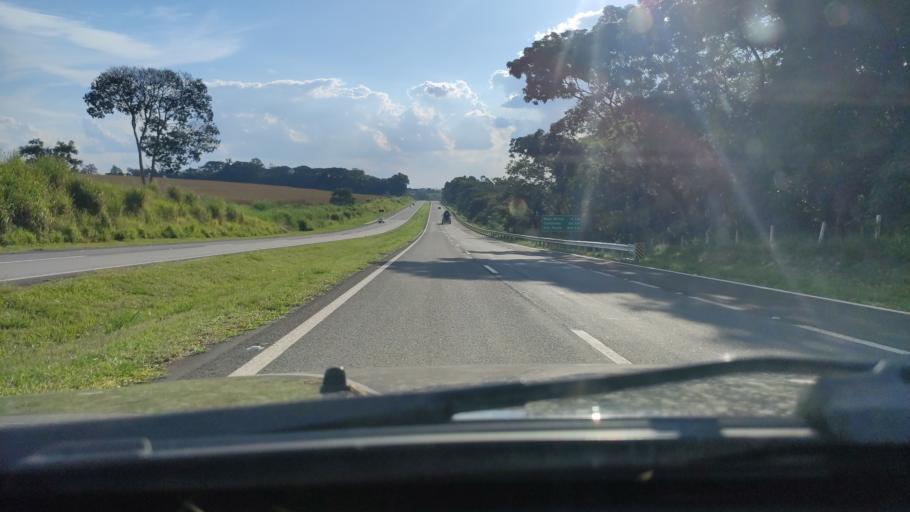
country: BR
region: Sao Paulo
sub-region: Itapira
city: Itapira
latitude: -22.4533
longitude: -46.8616
